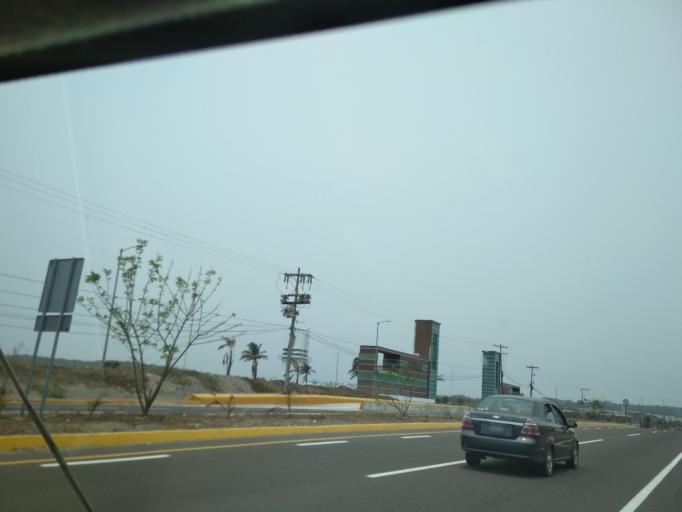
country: MX
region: Veracruz
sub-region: Alvarado
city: Playa de la Libertad
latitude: 19.0564
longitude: -96.0582
